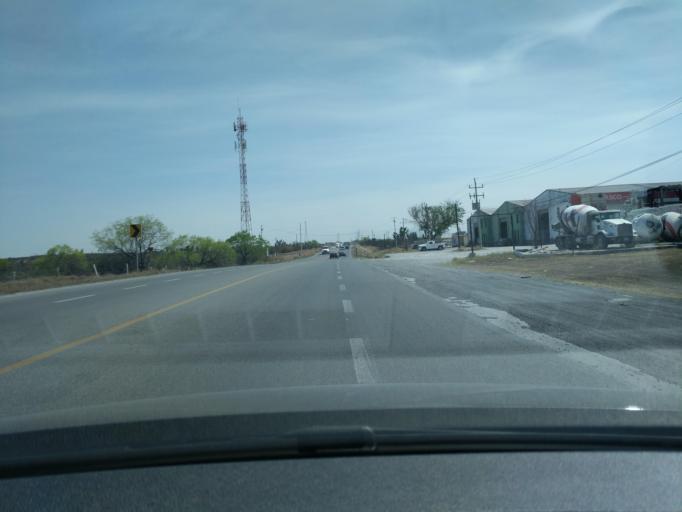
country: MX
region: Nuevo Leon
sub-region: Salinas Victoria
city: Las Torres
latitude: 25.9145
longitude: -100.3638
